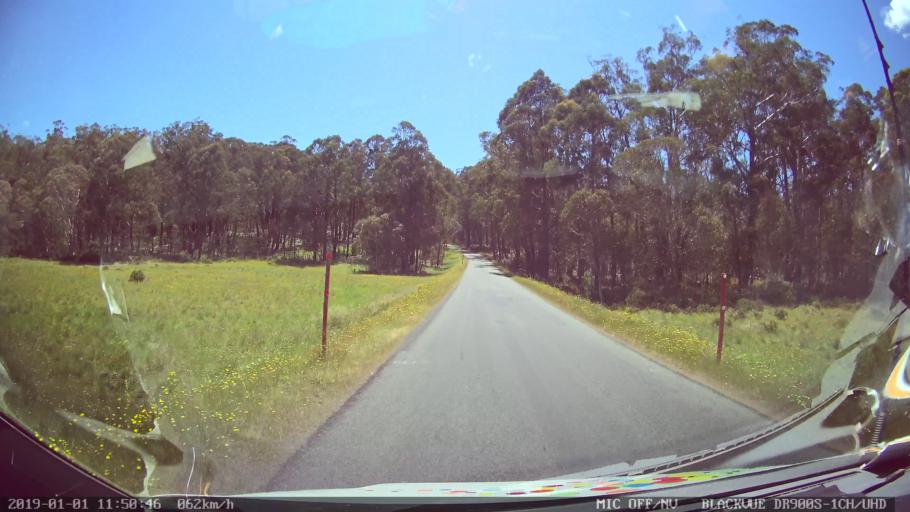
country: AU
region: New South Wales
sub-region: Snowy River
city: Jindabyne
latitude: -35.8895
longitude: 148.4240
